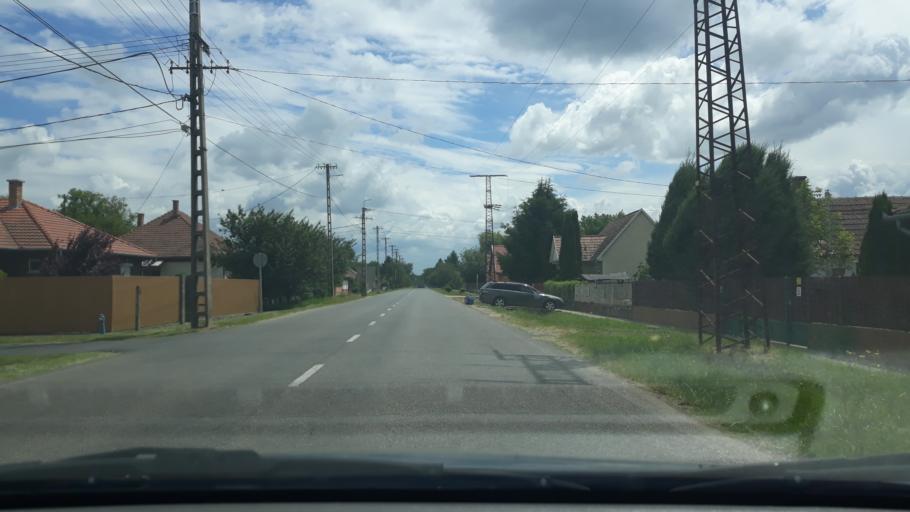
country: HU
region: Hajdu-Bihar
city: Biharkeresztes
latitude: 47.1311
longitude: 21.7319
